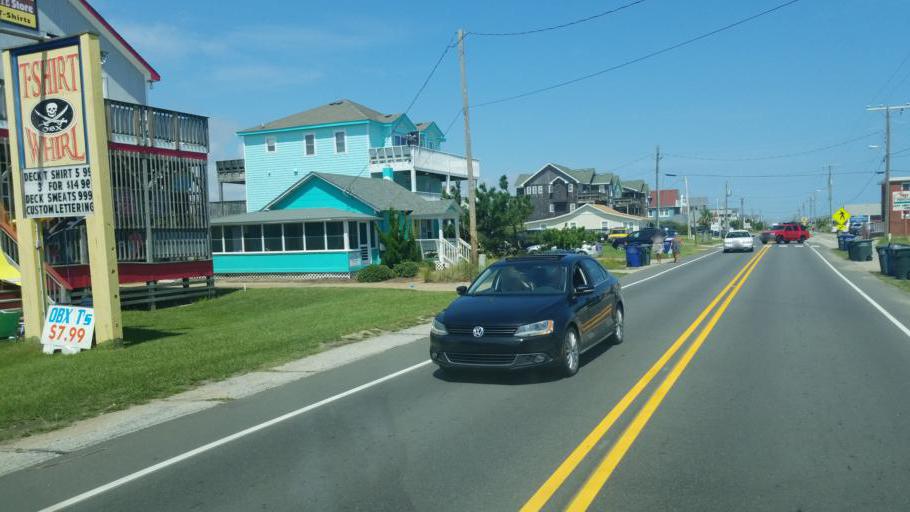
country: US
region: North Carolina
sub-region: Dare County
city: Nags Head
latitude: 35.9720
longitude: -75.6324
